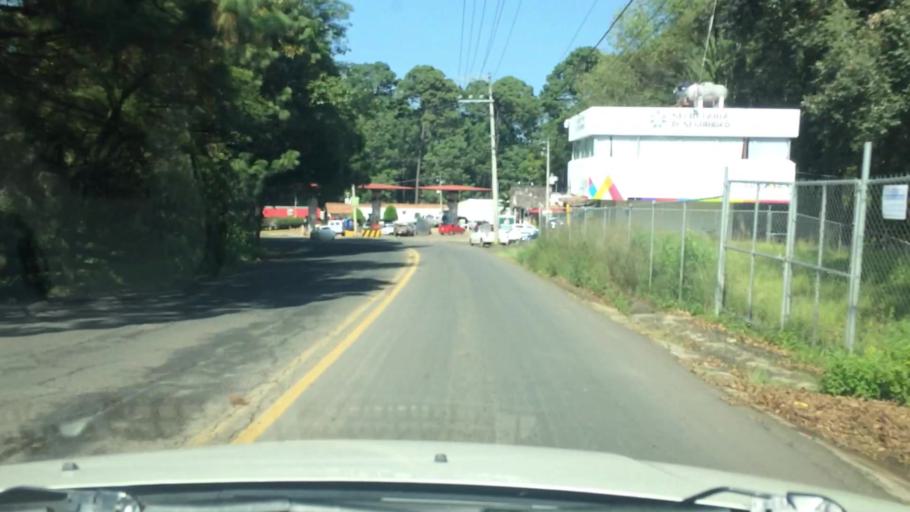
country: MX
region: Mexico
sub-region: Valle de Bravo
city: Casas Viejas
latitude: 19.1611
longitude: -100.1051
